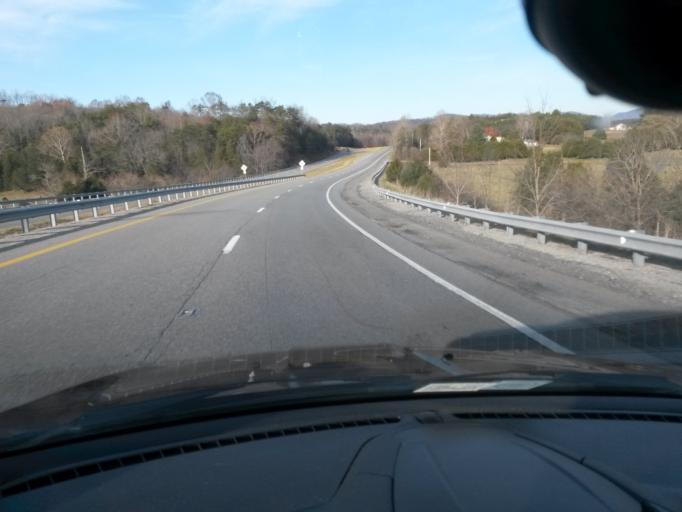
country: US
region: Virginia
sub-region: Botetourt County
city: Fincastle
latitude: 37.5613
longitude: -79.8465
